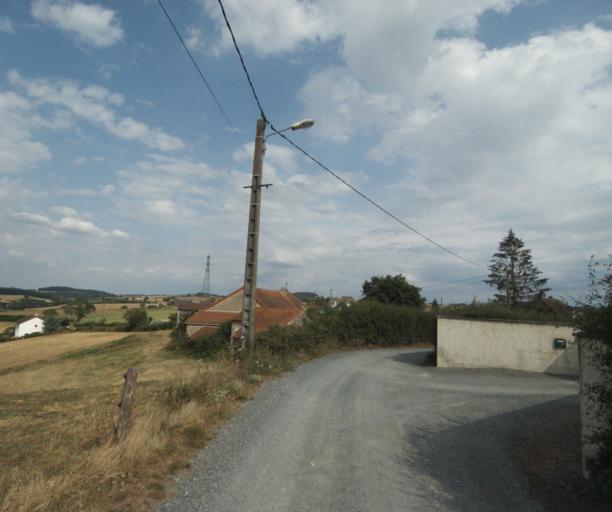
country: FR
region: Bourgogne
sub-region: Departement de Saone-et-Loire
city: Gueugnon
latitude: 46.6040
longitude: 4.0824
